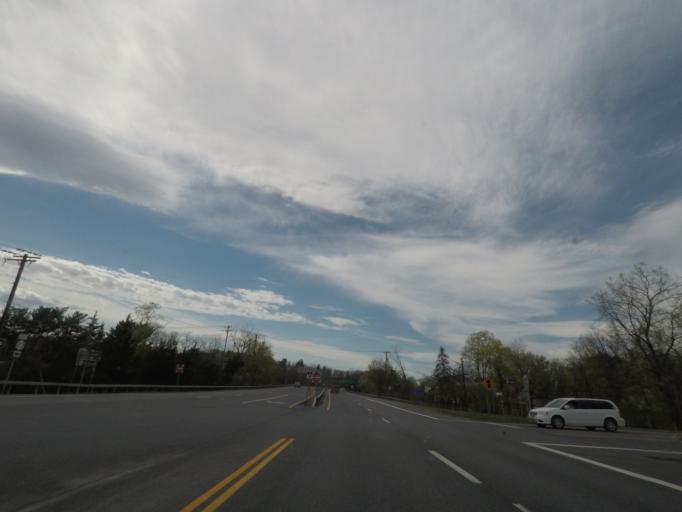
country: US
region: New York
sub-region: Greene County
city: Catskill
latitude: 42.2303
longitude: -73.8678
